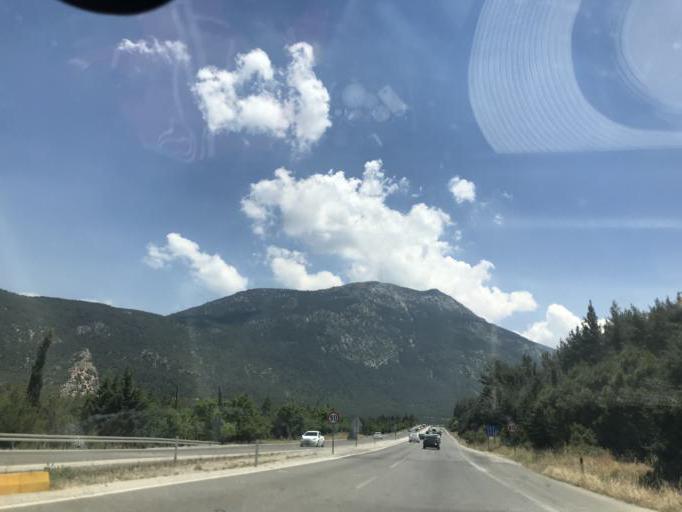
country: TR
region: Denizli
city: Honaz
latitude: 37.7280
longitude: 29.1983
